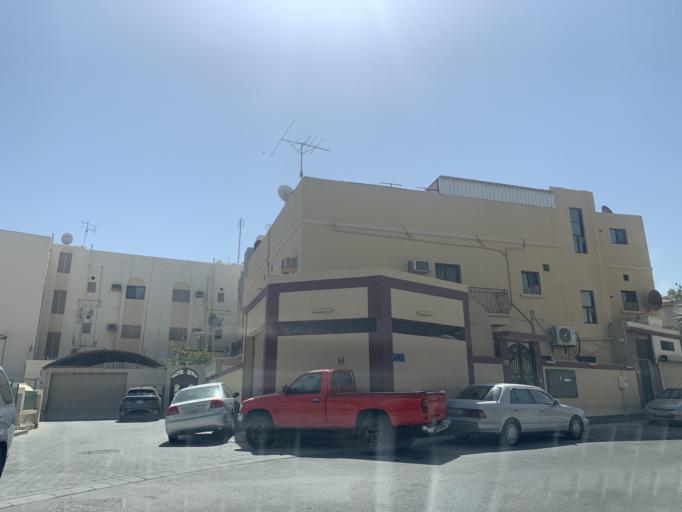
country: BH
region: Manama
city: Jidd Hafs
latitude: 26.2231
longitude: 50.5345
